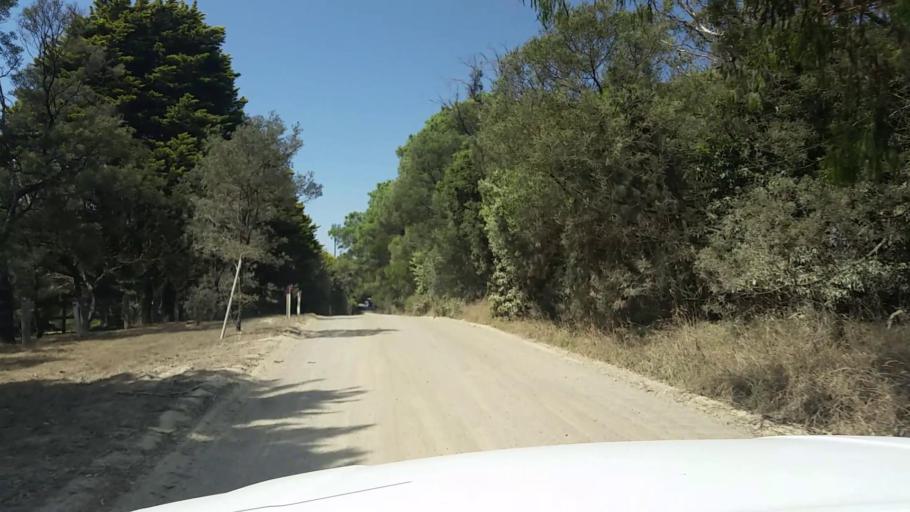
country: AU
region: Victoria
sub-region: Mornington Peninsula
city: Mount Martha
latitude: -38.2851
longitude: 145.0276
